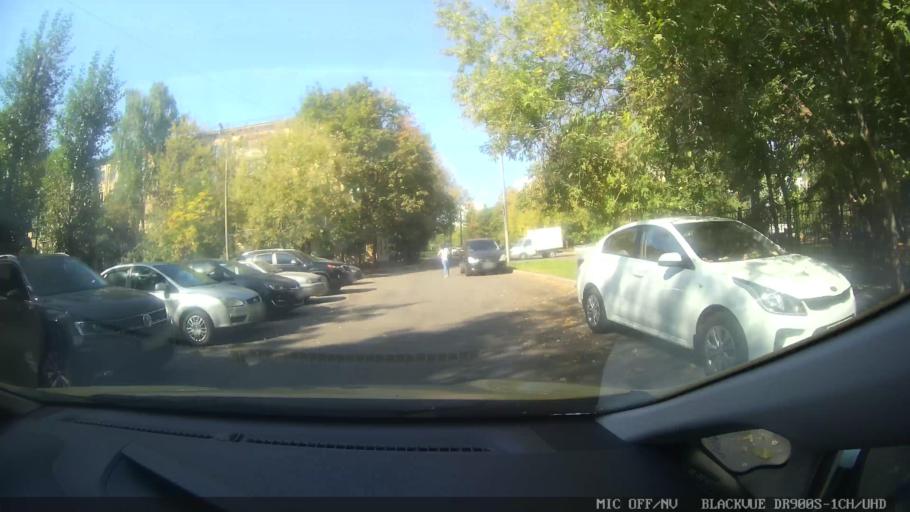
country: RU
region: Moscow
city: Novokuz'minki
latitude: 55.7006
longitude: 37.7805
